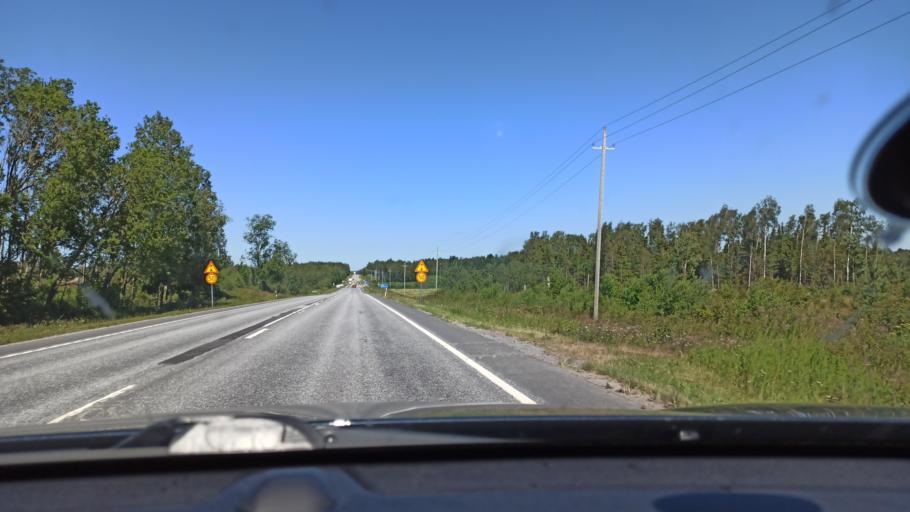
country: FI
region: Ostrobothnia
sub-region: Vaasa
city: Voera
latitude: 63.2354
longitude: 22.2522
